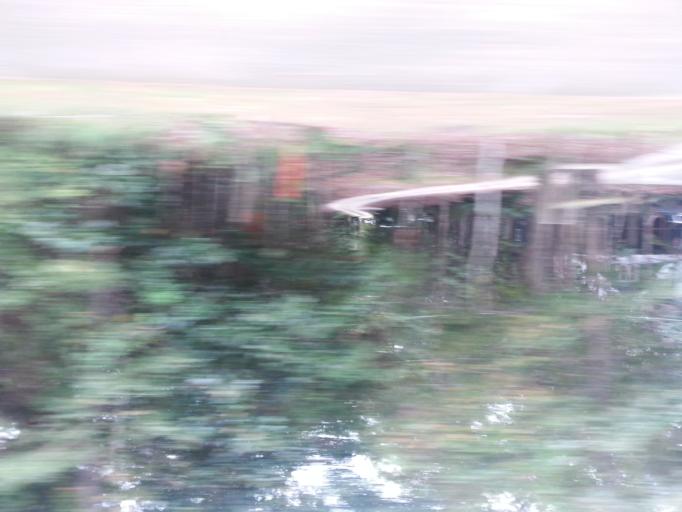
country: US
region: Alabama
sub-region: Baldwin County
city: Point Clear
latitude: 30.4693
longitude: -87.9172
